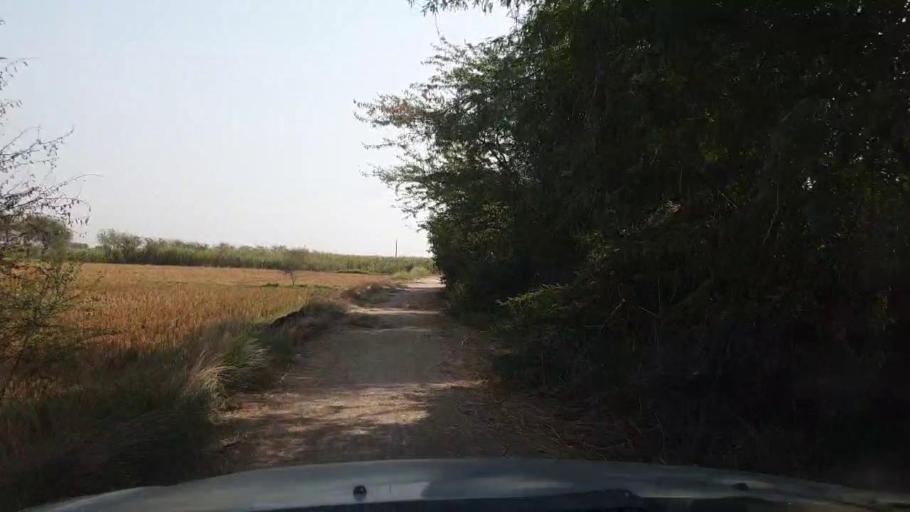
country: PK
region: Sindh
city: Bulri
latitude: 24.8923
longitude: 68.3755
